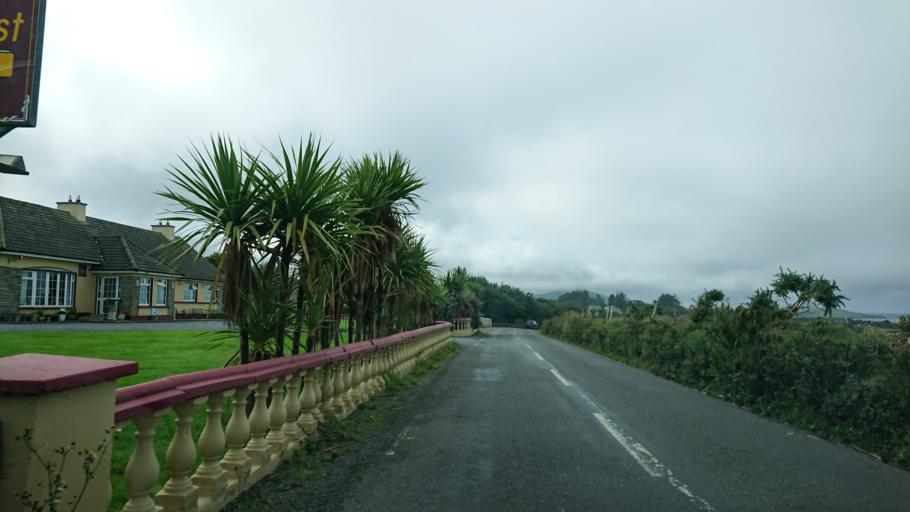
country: IE
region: Munster
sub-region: Ciarrai
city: Cahersiveen
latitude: 51.9326
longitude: -10.2459
